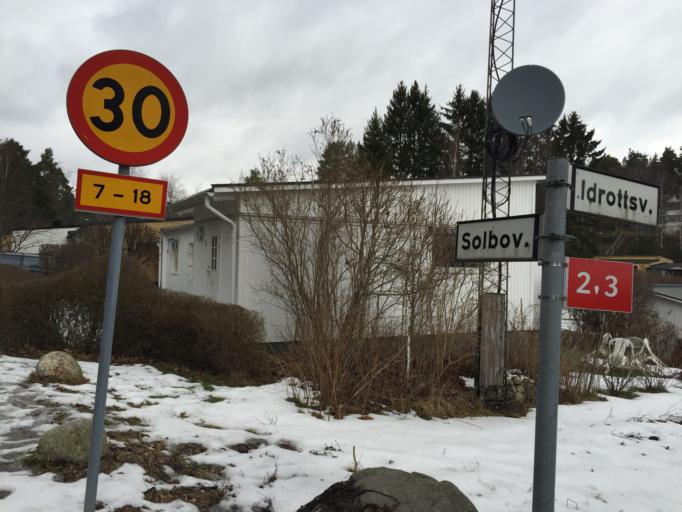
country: SE
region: Stockholm
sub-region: Salems Kommun
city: Ronninge
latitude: 59.2013
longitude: 17.7325
